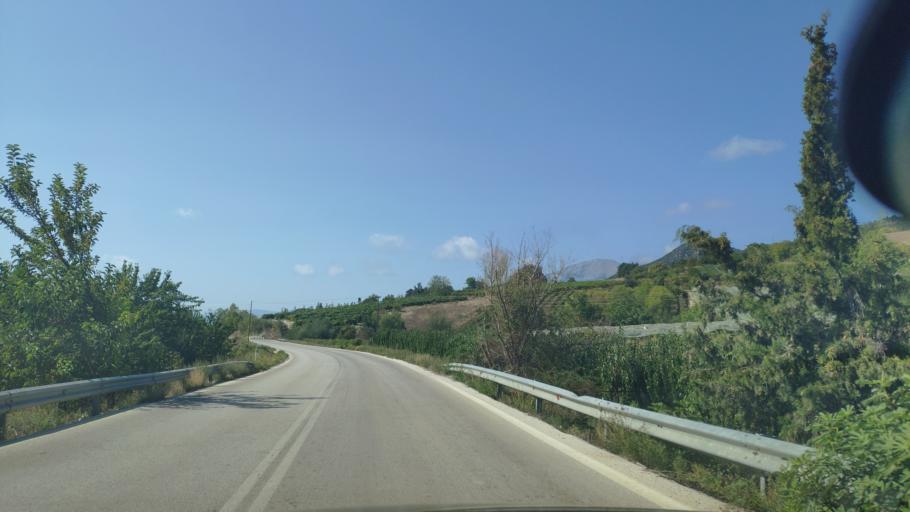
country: GR
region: Peloponnese
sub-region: Nomos Korinthias
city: Xylokastro
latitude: 37.9669
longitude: 22.5859
